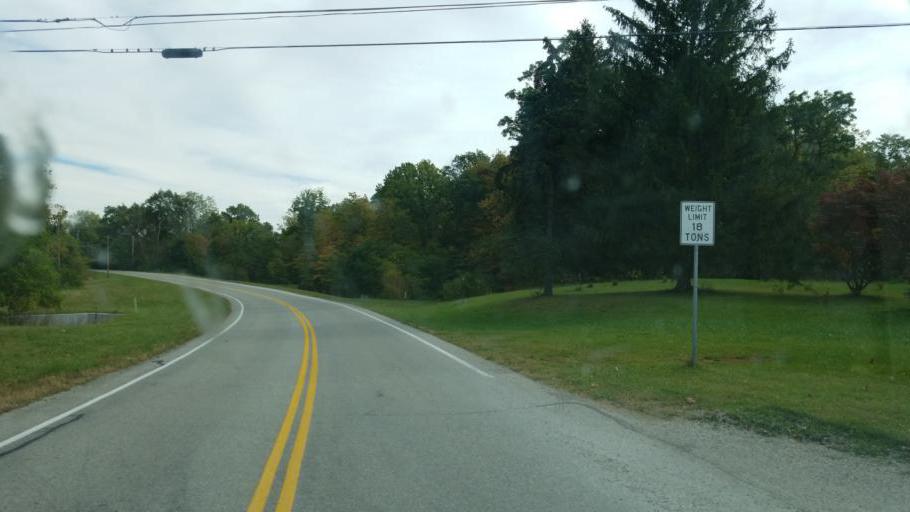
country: US
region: Ohio
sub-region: Lorain County
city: Vermilion
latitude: 41.3619
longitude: -82.4104
